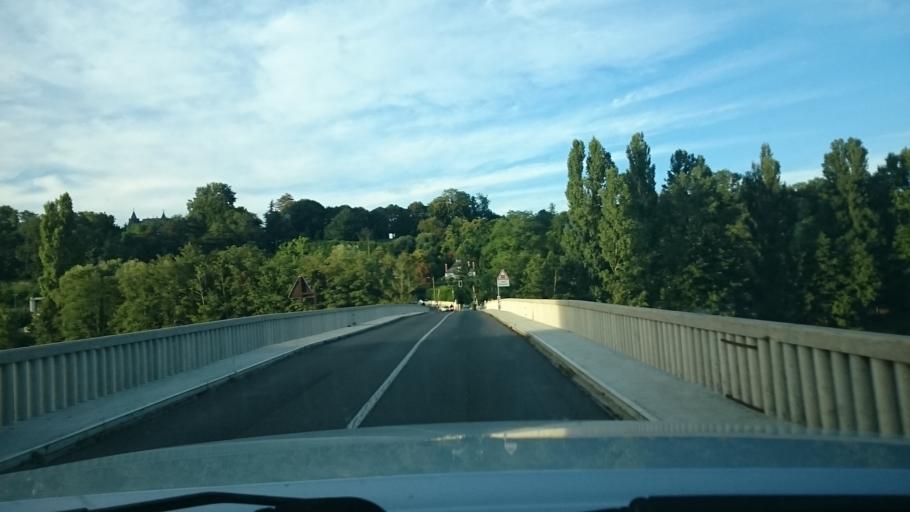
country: FR
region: Ile-de-France
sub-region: Departement de Seine-et-Marne
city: Samois-sur-Seine
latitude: 48.4853
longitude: 2.7519
